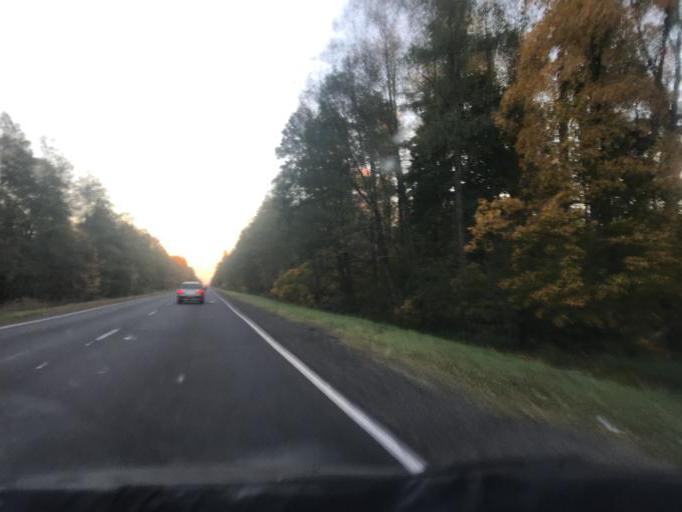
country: BY
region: Gomel
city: Mazyr
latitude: 52.1767
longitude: 29.1804
